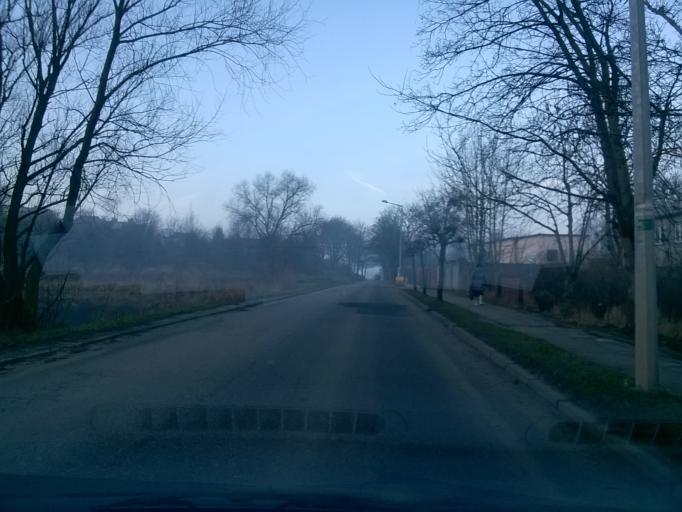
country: PL
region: Kujawsko-Pomorskie
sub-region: Powiat nakielski
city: Kcynia
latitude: 52.9944
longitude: 17.4925
